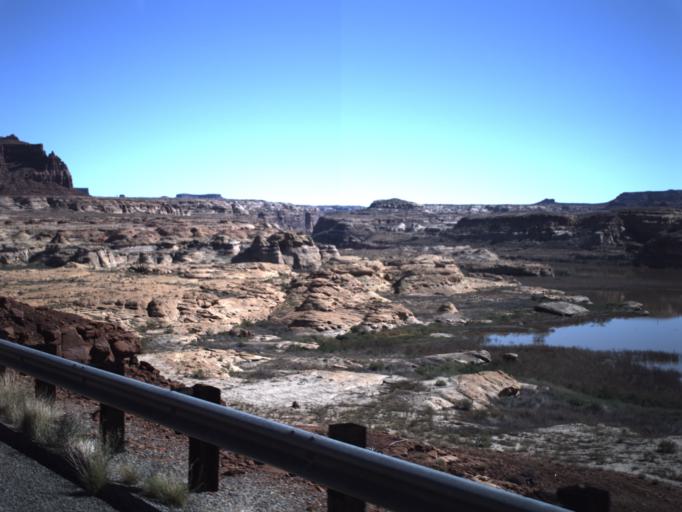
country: US
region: Utah
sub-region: San Juan County
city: Blanding
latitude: 37.8912
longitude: -110.3985
